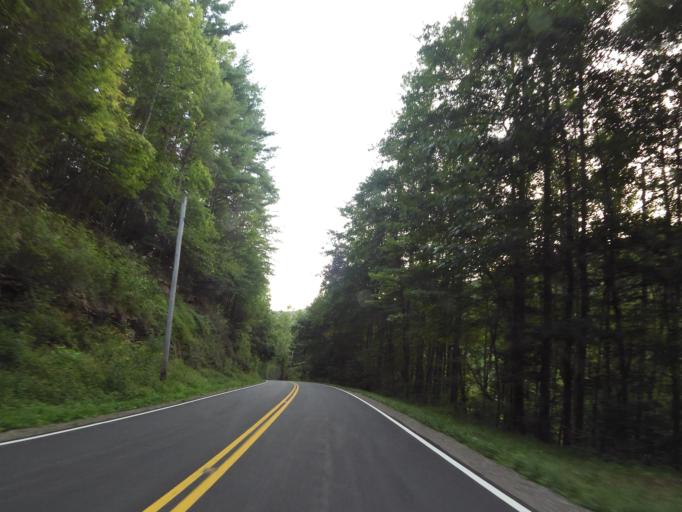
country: US
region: Tennessee
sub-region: Johnson County
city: Mountain City
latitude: 36.6115
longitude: -81.8077
